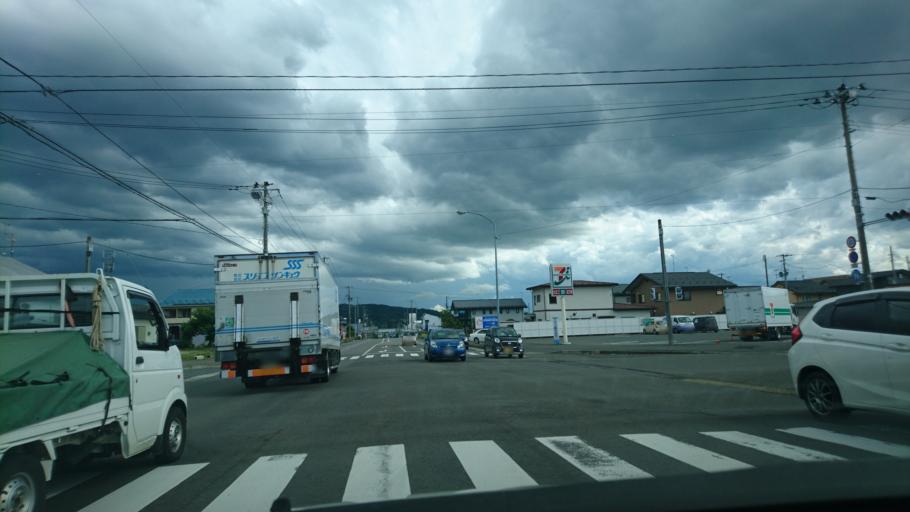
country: JP
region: Iwate
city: Kitakami
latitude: 39.3003
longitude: 141.1286
